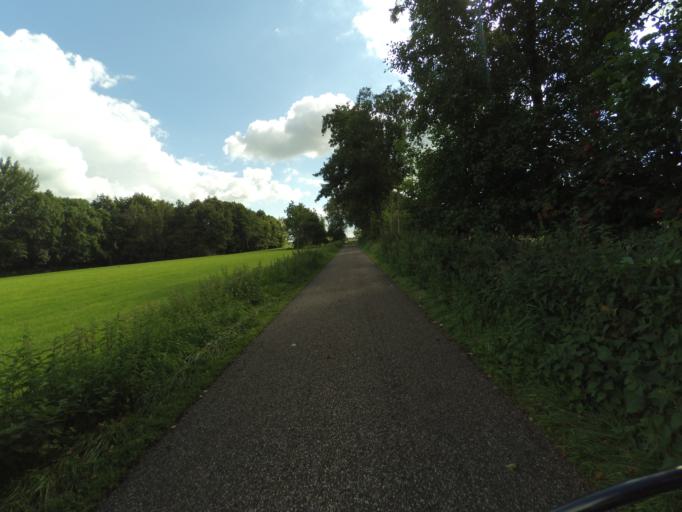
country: NL
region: Friesland
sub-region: Gemeente Tytsjerksteradiel
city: Tytsjerk
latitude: 53.2327
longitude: 5.9226
